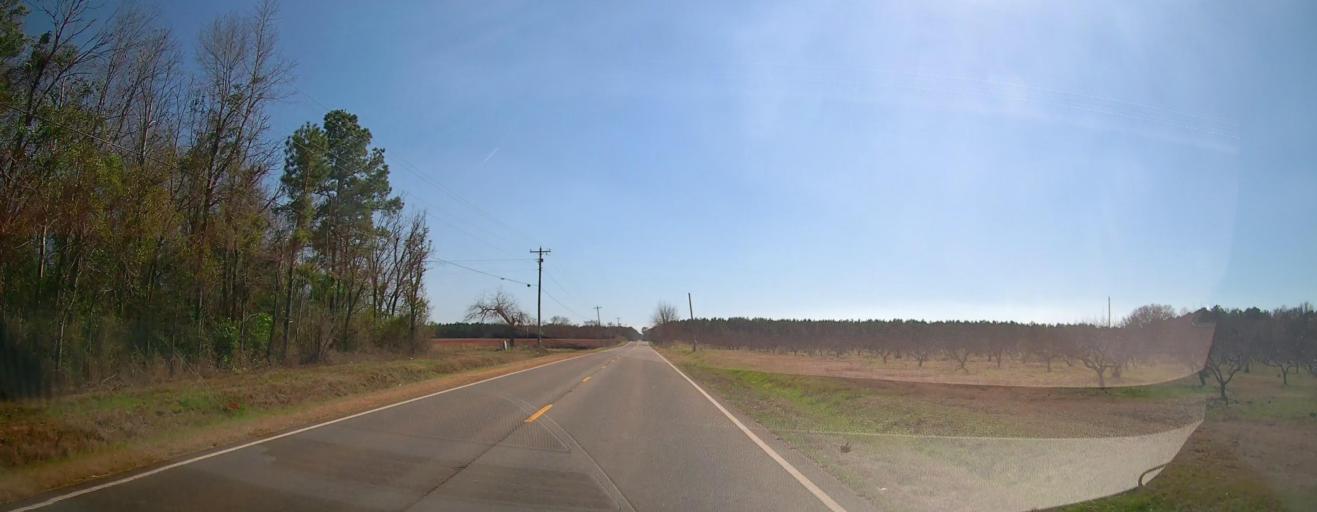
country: US
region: Georgia
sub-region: Macon County
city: Montezuma
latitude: 32.3310
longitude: -84.0216
